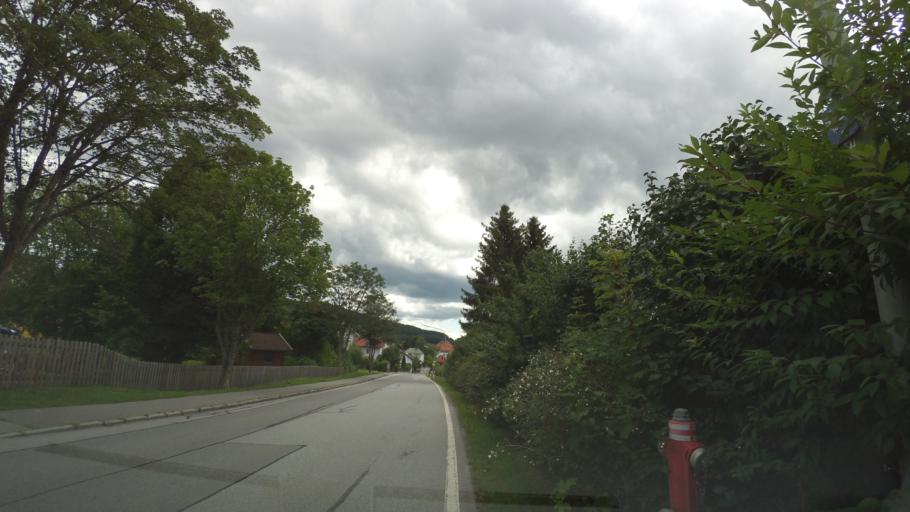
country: DE
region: Bavaria
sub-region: Lower Bavaria
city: Bodenmais
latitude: 49.0686
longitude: 13.0950
